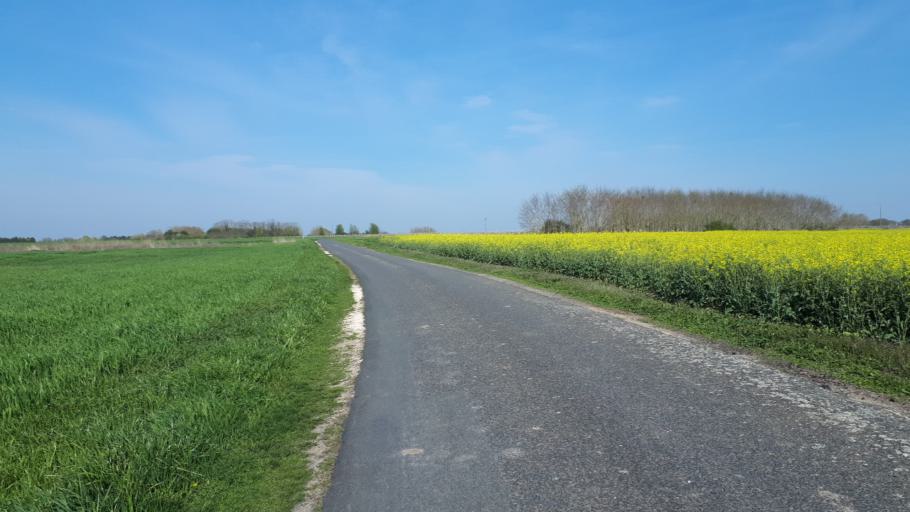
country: FR
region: Centre
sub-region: Departement du Loir-et-Cher
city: Contres
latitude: 47.3848
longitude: 1.3886
